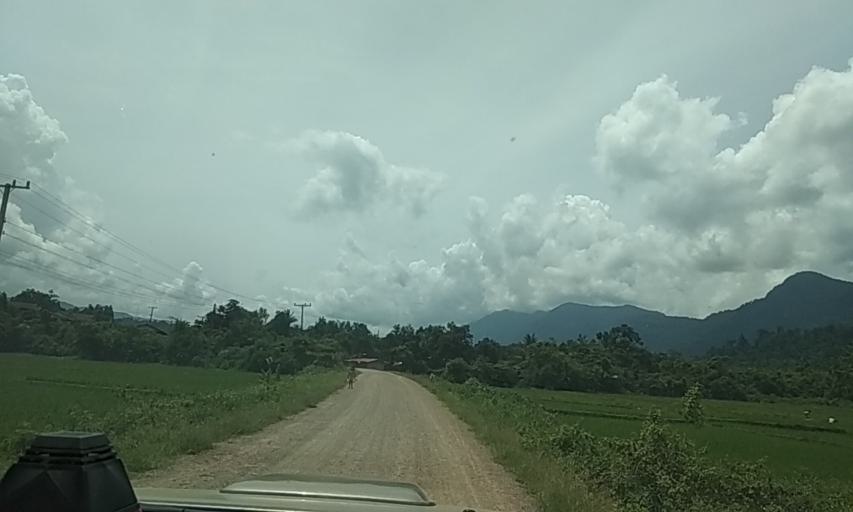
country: LA
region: Bolikhamxai
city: Ban Nahin
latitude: 18.1526
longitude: 104.7236
